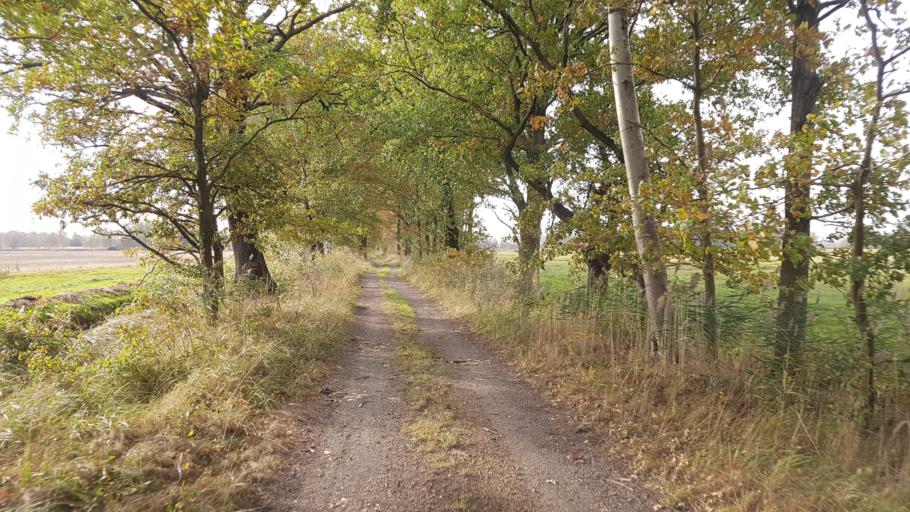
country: DE
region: Brandenburg
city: Schraden
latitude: 51.4520
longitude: 13.6986
